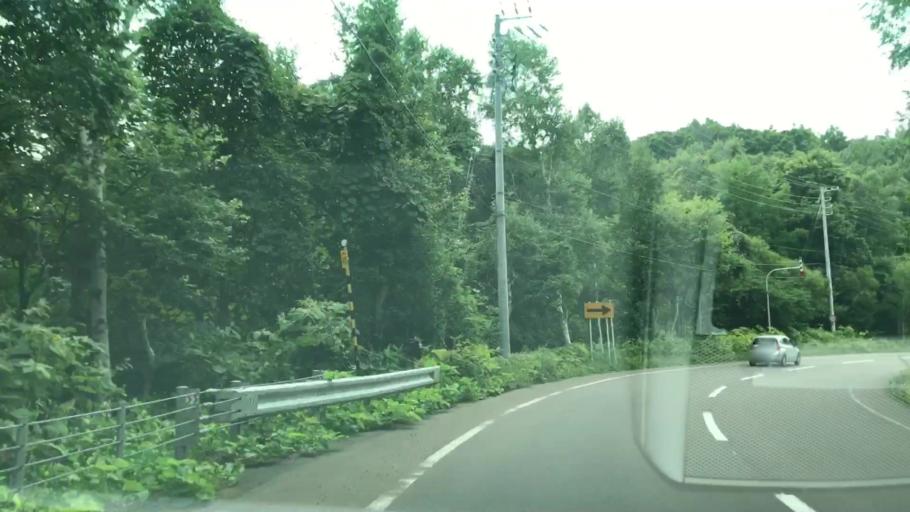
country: JP
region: Hokkaido
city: Yoichi
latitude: 43.1314
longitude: 140.8267
